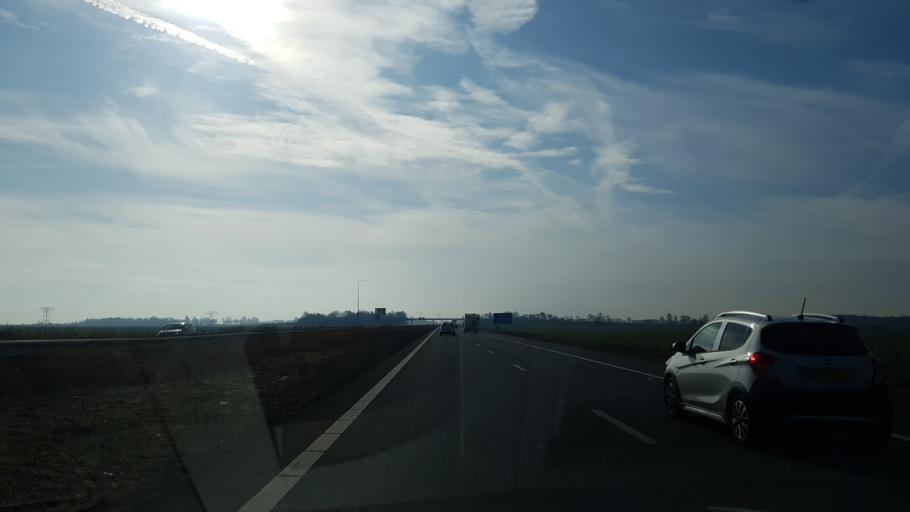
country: NL
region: Friesland
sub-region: Gemeente Skarsterlan
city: Sint Nicolaasga
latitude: 52.9308
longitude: 5.7822
